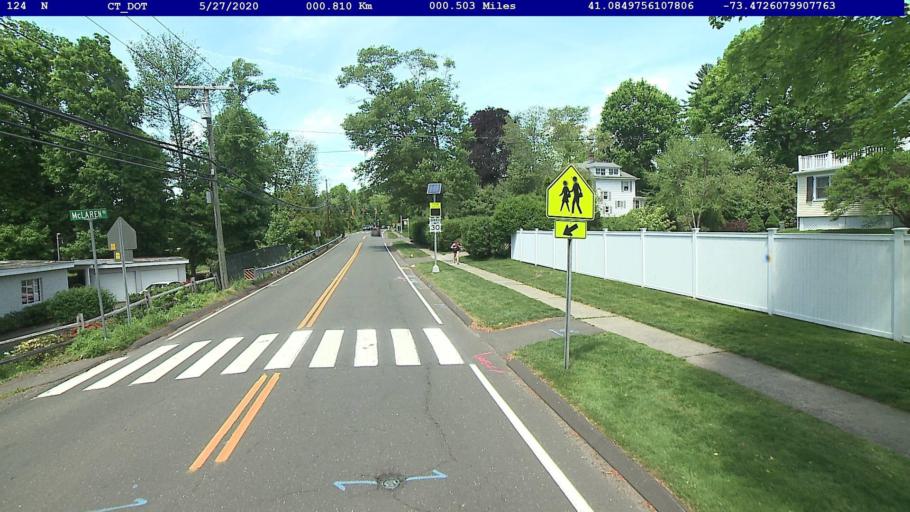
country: US
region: Connecticut
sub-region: Fairfield County
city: Darien
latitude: 41.0850
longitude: -73.4726
